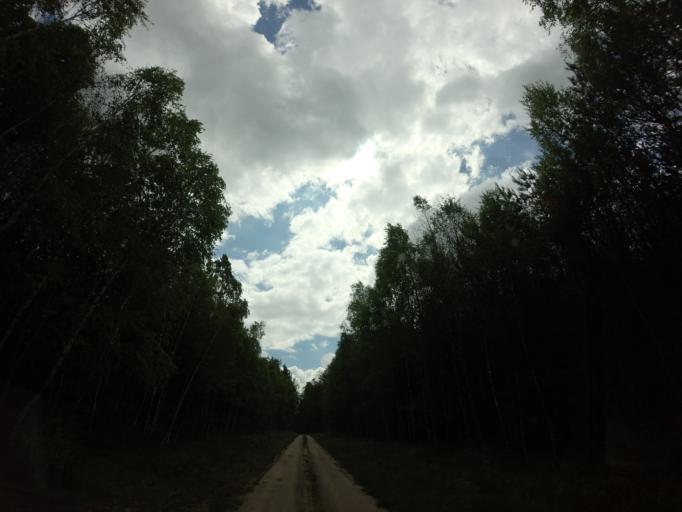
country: PL
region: West Pomeranian Voivodeship
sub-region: Powiat drawski
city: Kalisz Pomorski
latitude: 53.1640
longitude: 15.9052
